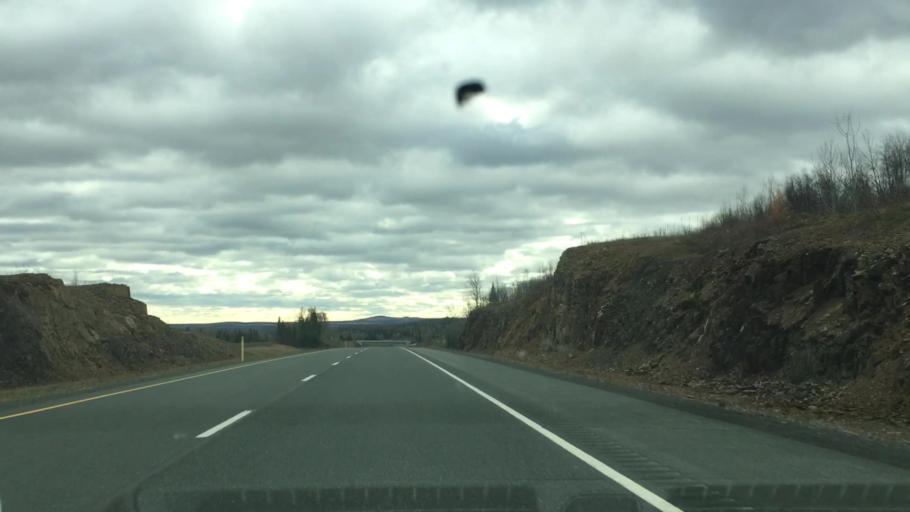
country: US
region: Maine
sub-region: Aroostook County
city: Fort Fairfield
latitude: 46.6328
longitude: -67.7422
